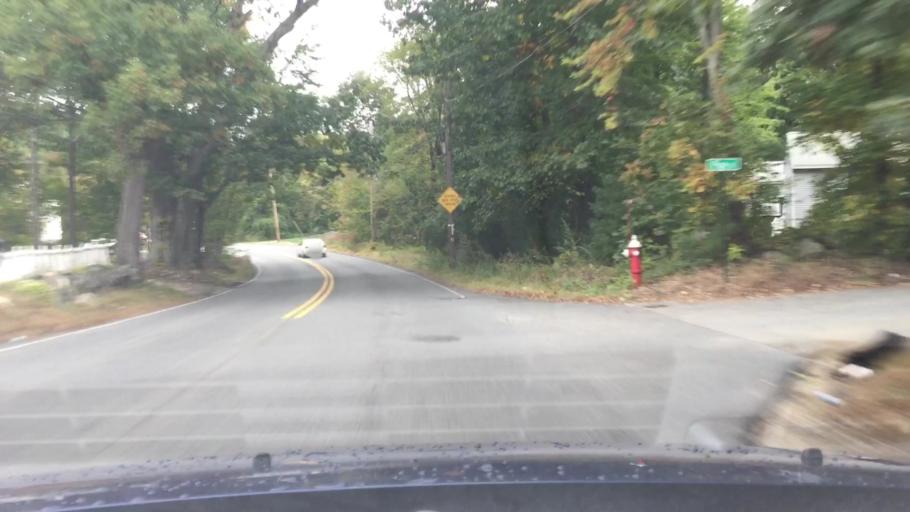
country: US
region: Massachusetts
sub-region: Middlesex County
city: Tyngsboro
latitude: 42.6880
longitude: -71.3751
